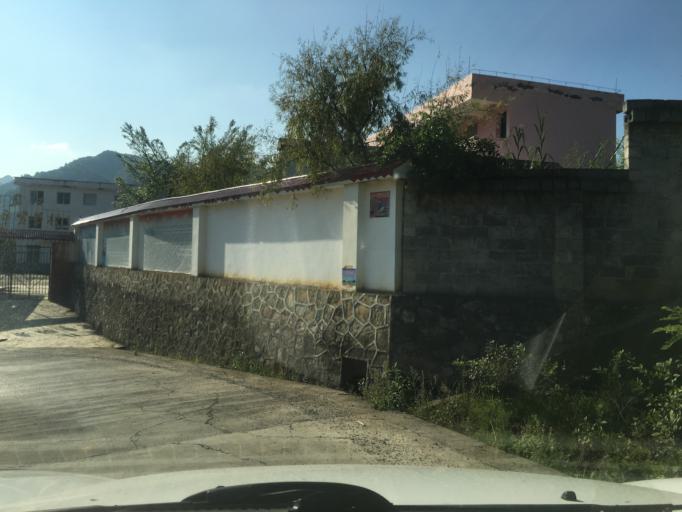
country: CN
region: Guangxi Zhuangzu Zizhiqu
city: Xinzhou
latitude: 25.4223
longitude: 105.7459
